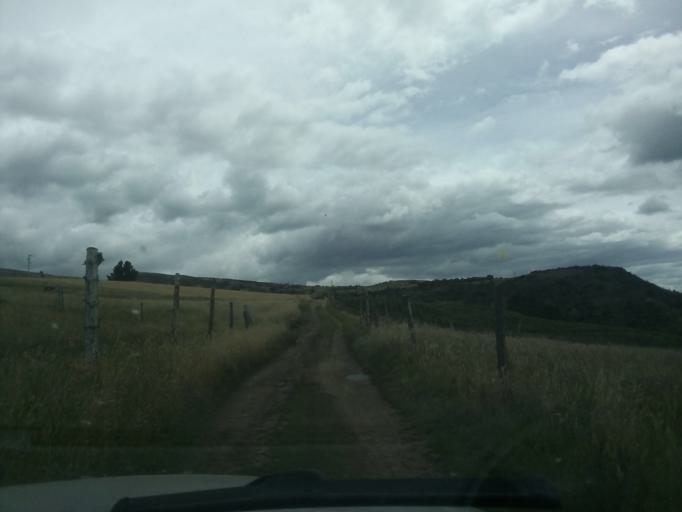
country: CO
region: Boyaca
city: Toca
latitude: 5.5972
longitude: -73.1174
